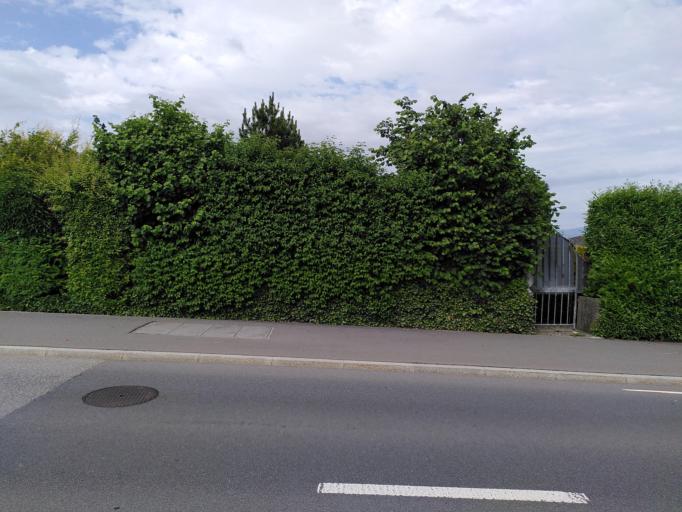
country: CH
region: Zurich
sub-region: Bezirk Horgen
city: Richterswil / Burghalde
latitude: 47.2067
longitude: 8.6920
